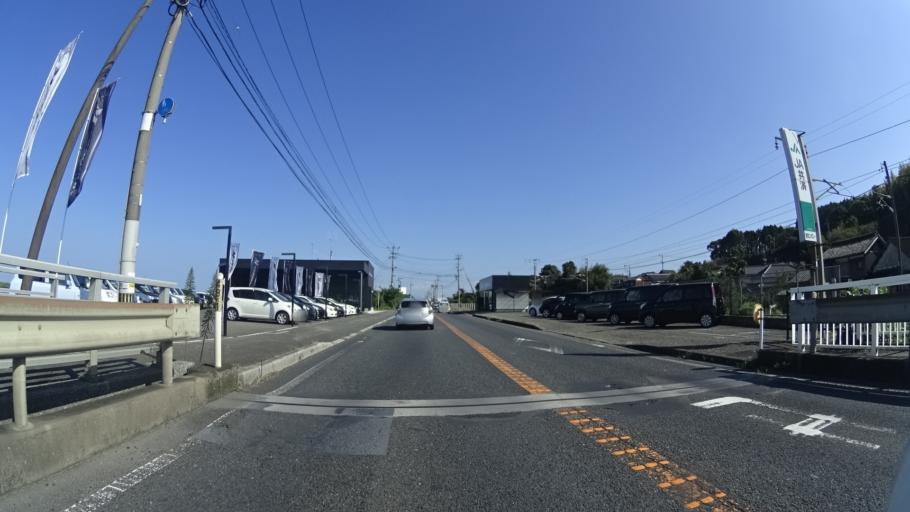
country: JP
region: Fukuoka
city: Shiida
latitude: 33.6363
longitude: 131.0737
